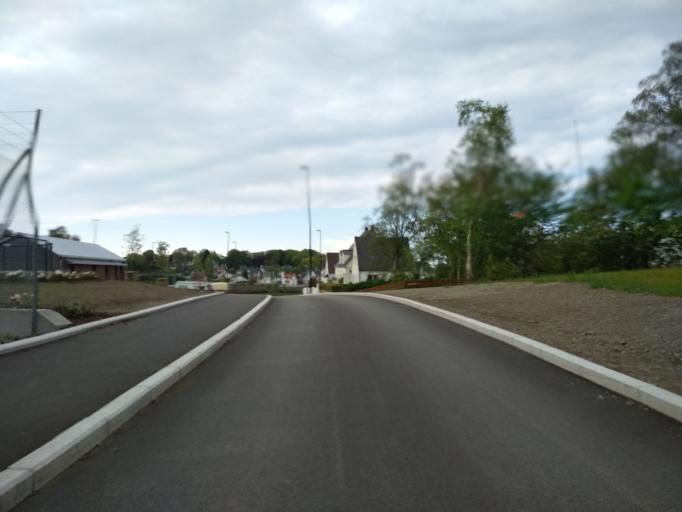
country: NO
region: Rogaland
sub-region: Stavanger
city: Stavanger
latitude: 58.9583
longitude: 5.7238
